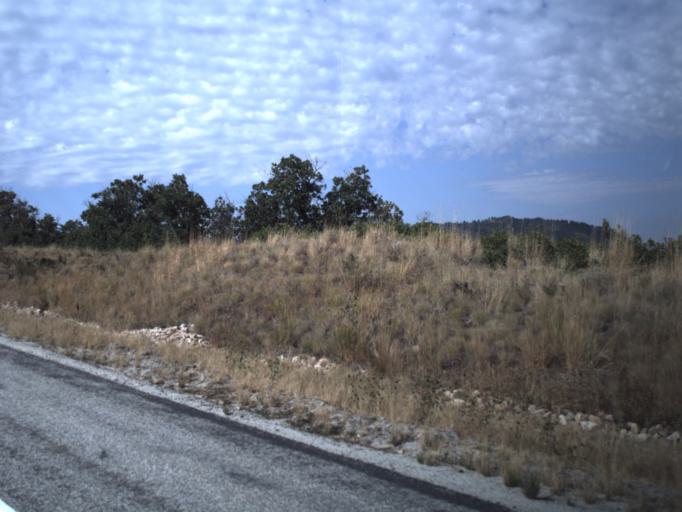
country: US
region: Utah
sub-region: Morgan County
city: Mountain Green
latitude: 41.2098
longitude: -111.8416
